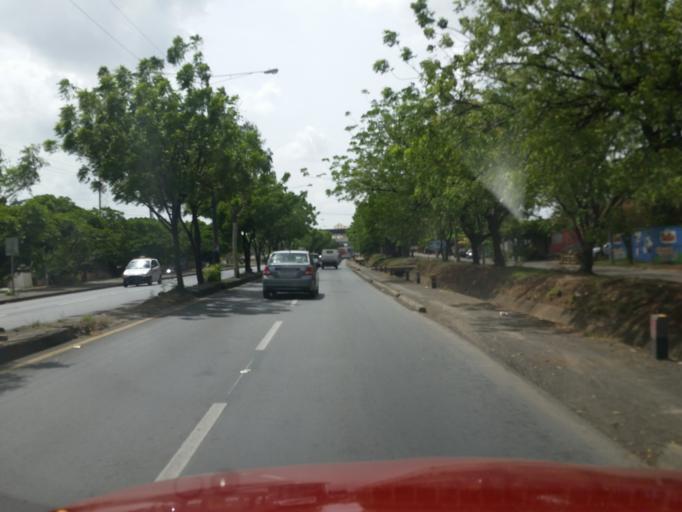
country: NI
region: Managua
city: Managua
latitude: 12.1258
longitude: -86.2867
